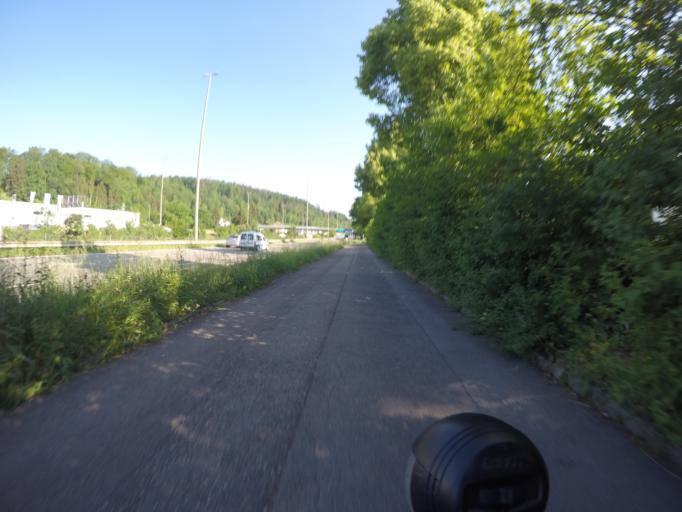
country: CH
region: Zurich
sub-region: Bezirk Winterthur
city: Toss
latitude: 47.4822
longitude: 8.7043
